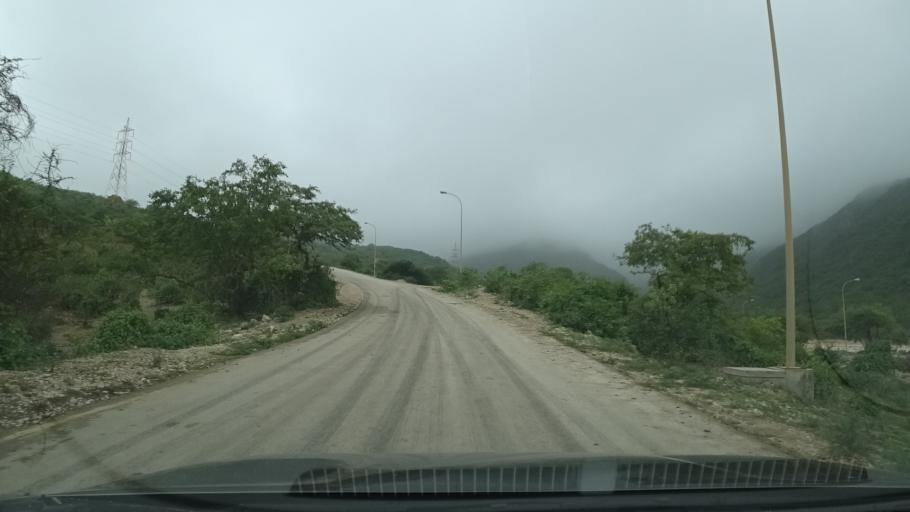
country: OM
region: Zufar
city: Salalah
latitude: 17.1014
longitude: 54.0765
